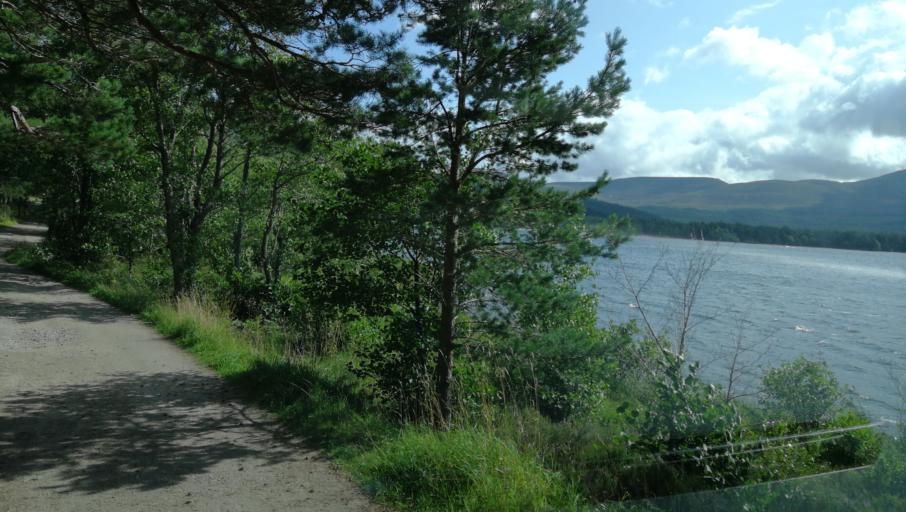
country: GB
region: Scotland
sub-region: Highland
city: Aviemore
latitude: 57.1668
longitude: -3.7152
